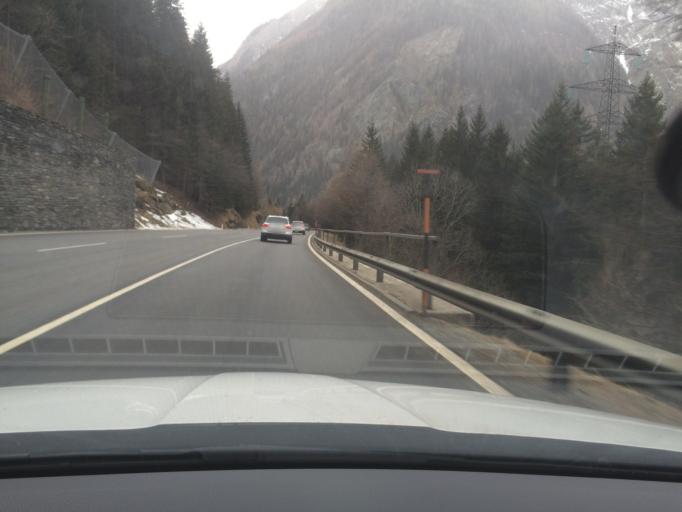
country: AT
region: Tyrol
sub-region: Politischer Bezirk Lienz
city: Matrei in Osttirol
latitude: 47.0495
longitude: 12.5174
